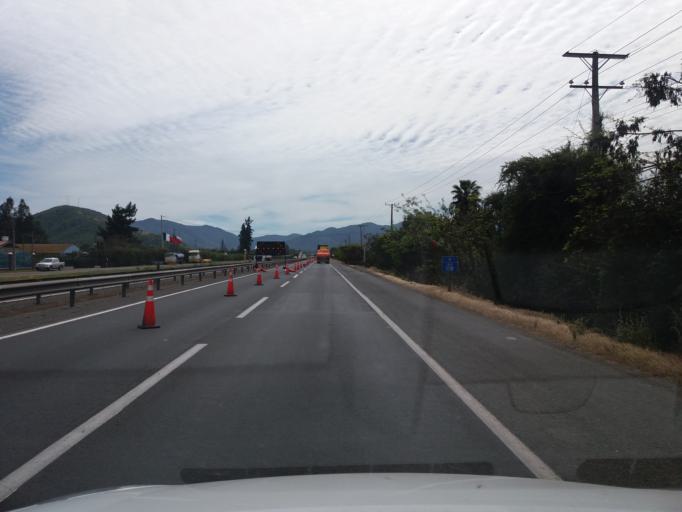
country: CL
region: Valparaiso
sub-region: Provincia de Quillota
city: Hacienda La Calera
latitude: -32.7147
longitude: -71.2047
